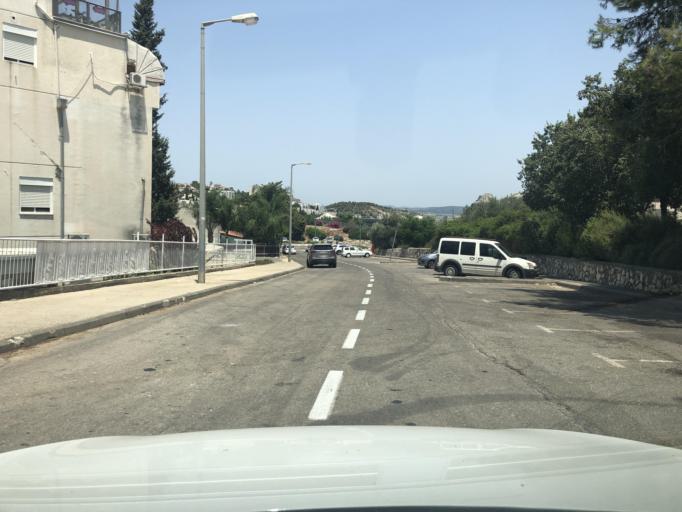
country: IL
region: Haifa
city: Daliyat el Karmil
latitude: 32.6446
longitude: 35.0908
